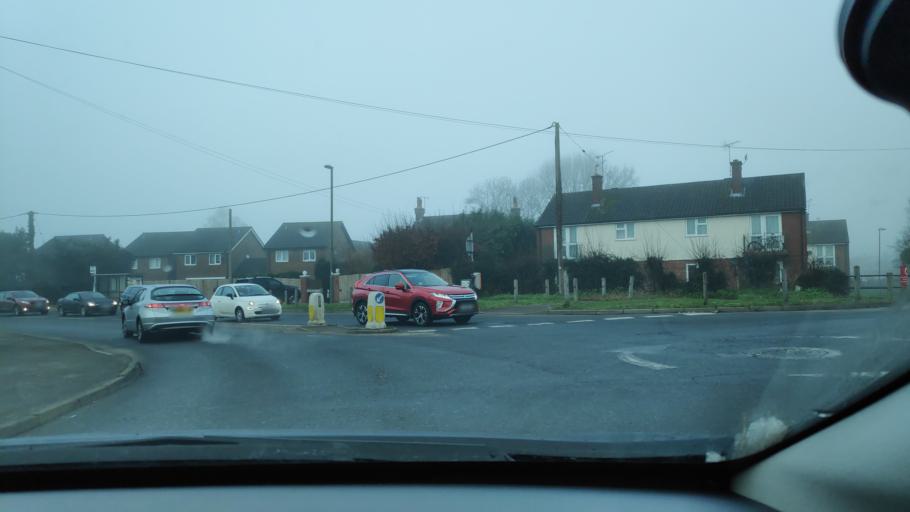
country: GB
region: England
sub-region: Surrey
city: Seale
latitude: 51.2513
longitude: -0.7109
